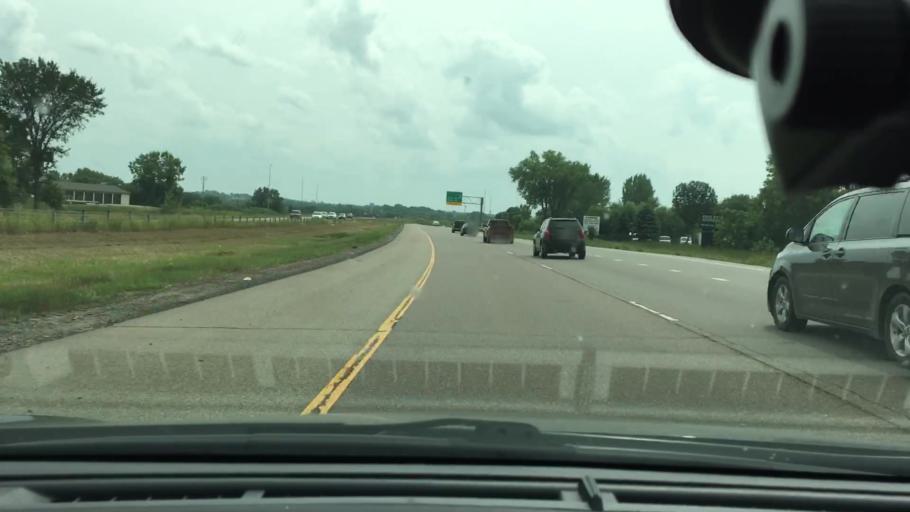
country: US
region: Minnesota
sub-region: Hennepin County
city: Dayton
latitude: 45.2358
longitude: -93.5549
